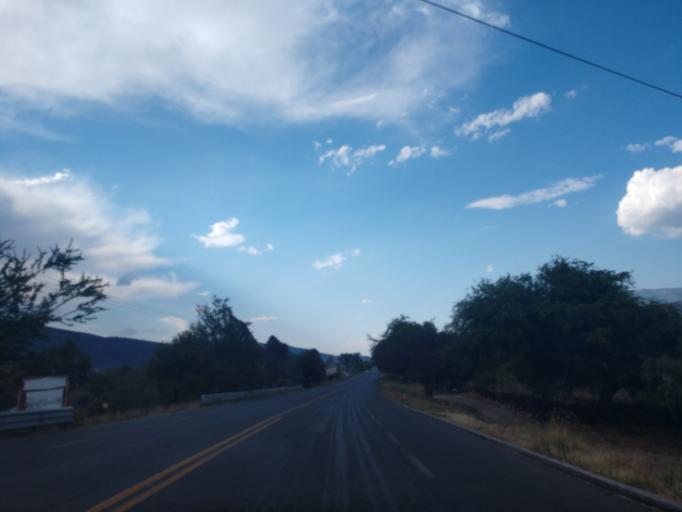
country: MX
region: Jalisco
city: Jocotepec
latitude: 20.2311
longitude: -103.4202
